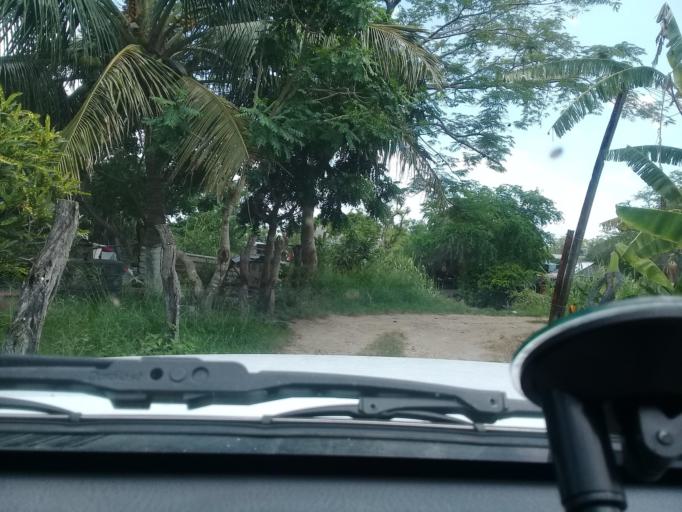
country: MX
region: Veracruz
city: Moralillo
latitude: 22.1823
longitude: -98.0179
